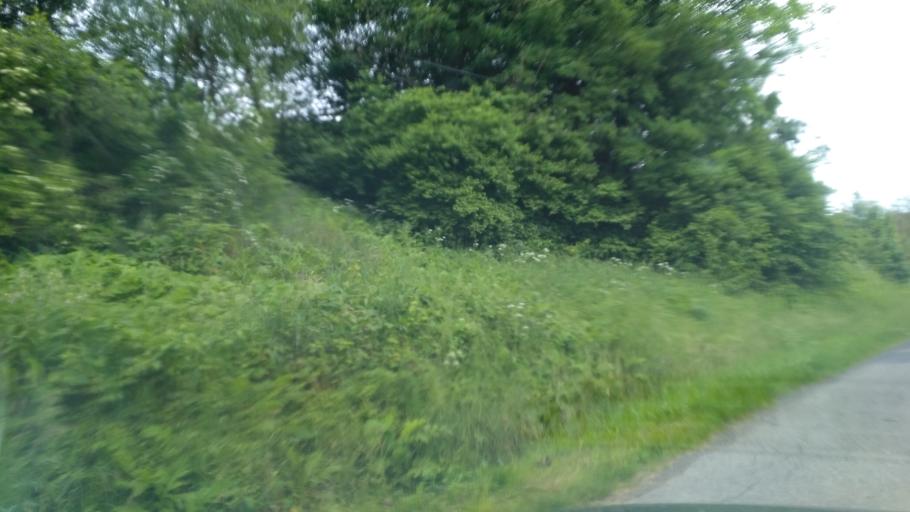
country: PL
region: Subcarpathian Voivodeship
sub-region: Powiat przemyski
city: Nienadowa
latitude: 49.8559
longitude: 22.4131
